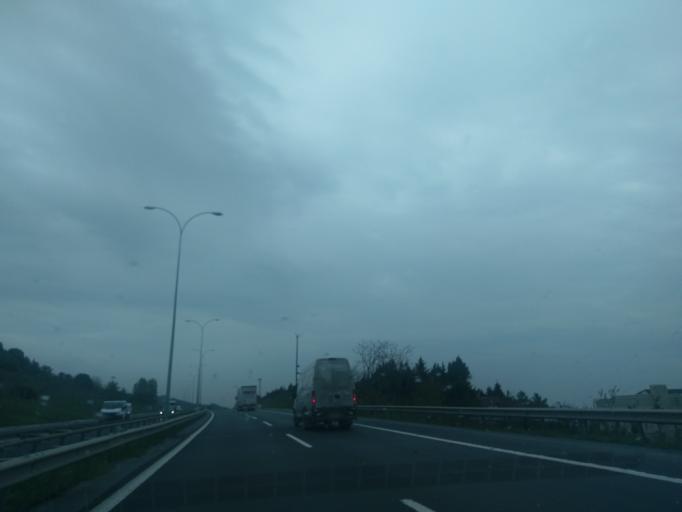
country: TR
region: Istanbul
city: Celaliye
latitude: 41.0578
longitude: 28.4162
